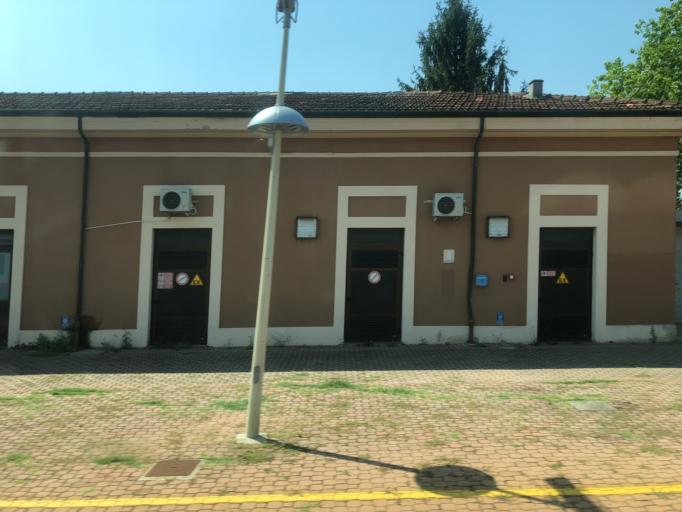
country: IT
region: Emilia-Romagna
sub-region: Provincia di Rimini
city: Santarcangelo
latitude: 44.0702
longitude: 12.4541
